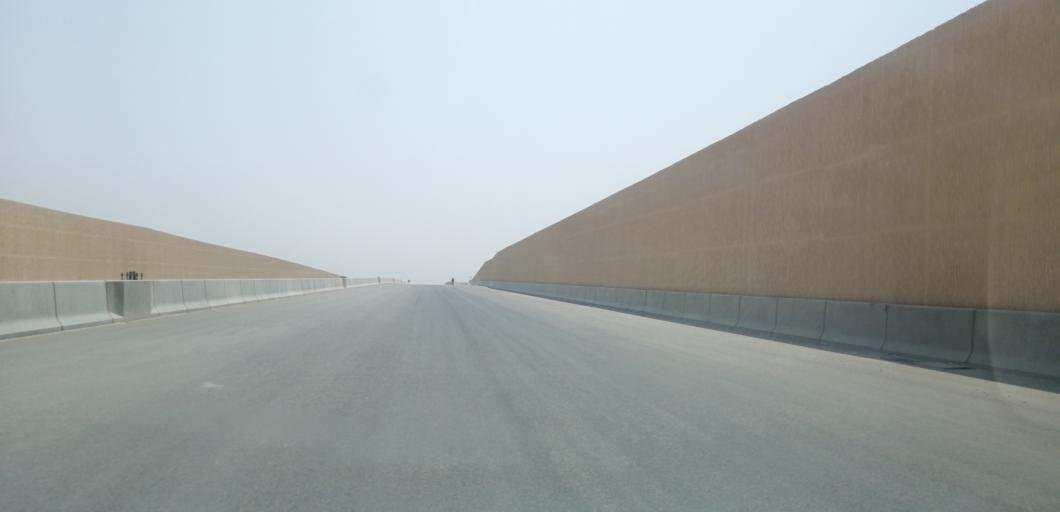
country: KW
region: Muhafazat al Jahra'
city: Al Jahra'
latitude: 29.4534
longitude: 47.5607
